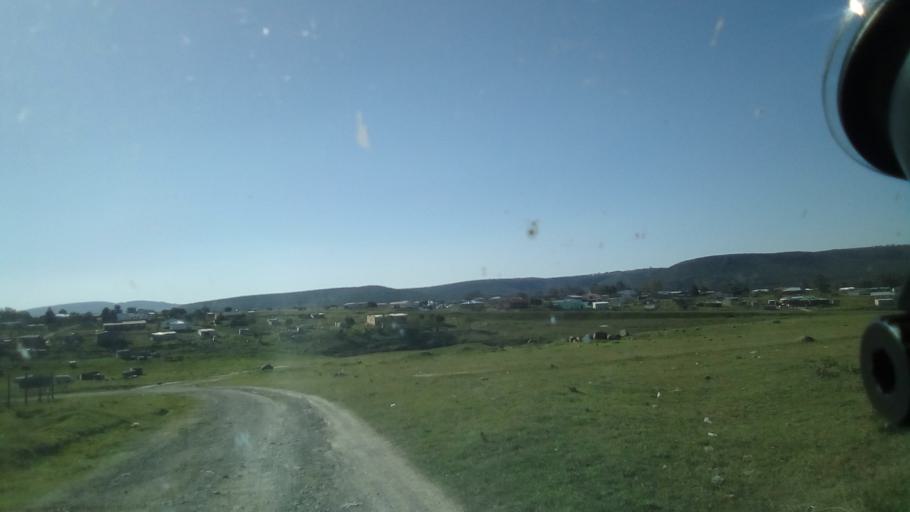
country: ZA
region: Eastern Cape
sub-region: Buffalo City Metropolitan Municipality
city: Bhisho
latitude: -32.8317
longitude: 27.3732
